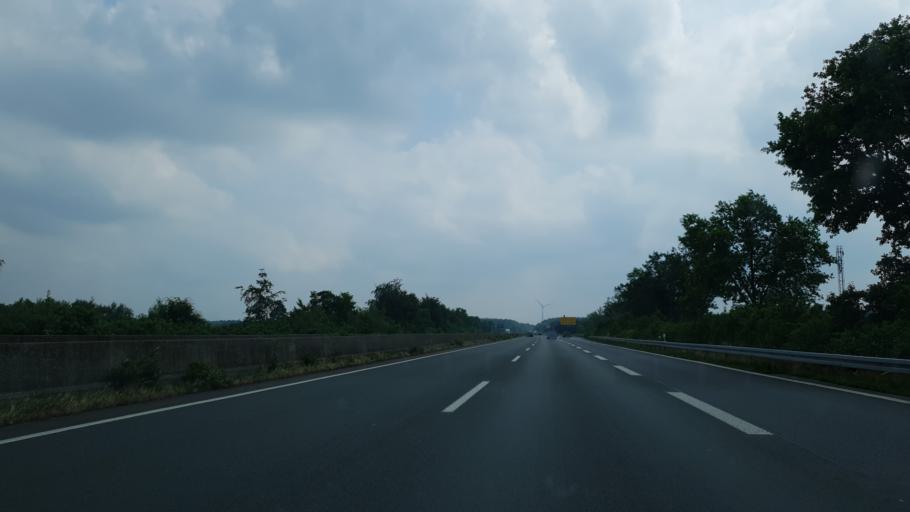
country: DE
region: North Rhine-Westphalia
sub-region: Regierungsbezirk Munster
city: Velen
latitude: 51.8602
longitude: 7.0064
